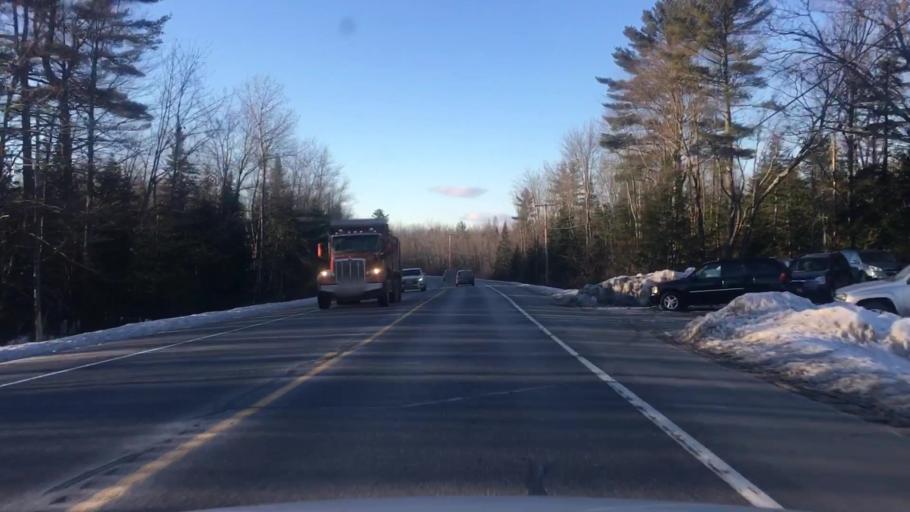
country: US
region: Maine
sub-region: Franklin County
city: New Sharon
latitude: 44.6442
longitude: -70.0228
